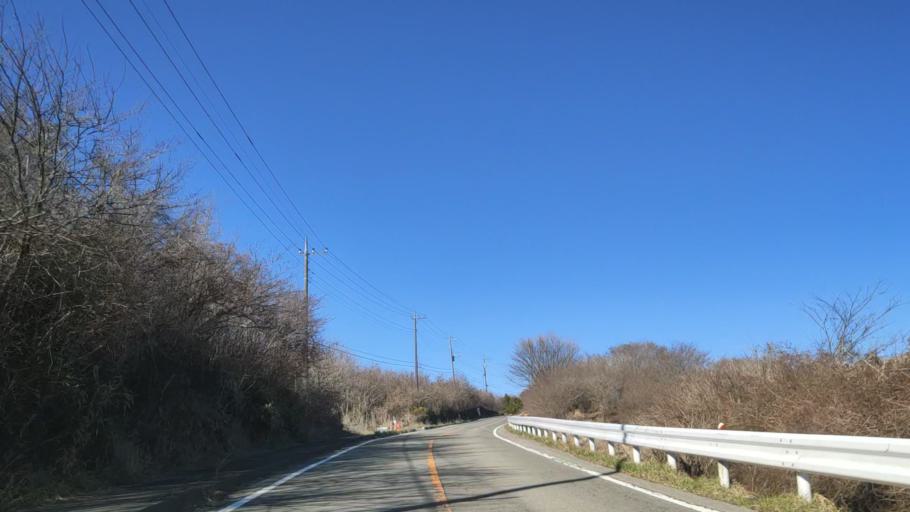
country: JP
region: Yamanashi
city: Fujikawaguchiko
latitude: 35.4097
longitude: 138.6179
